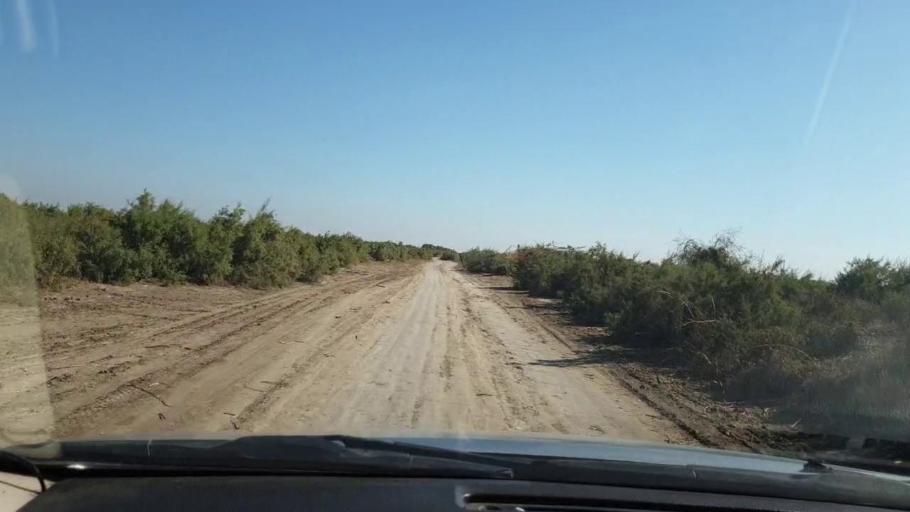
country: PK
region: Sindh
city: Berani
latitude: 25.7193
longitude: 68.9833
